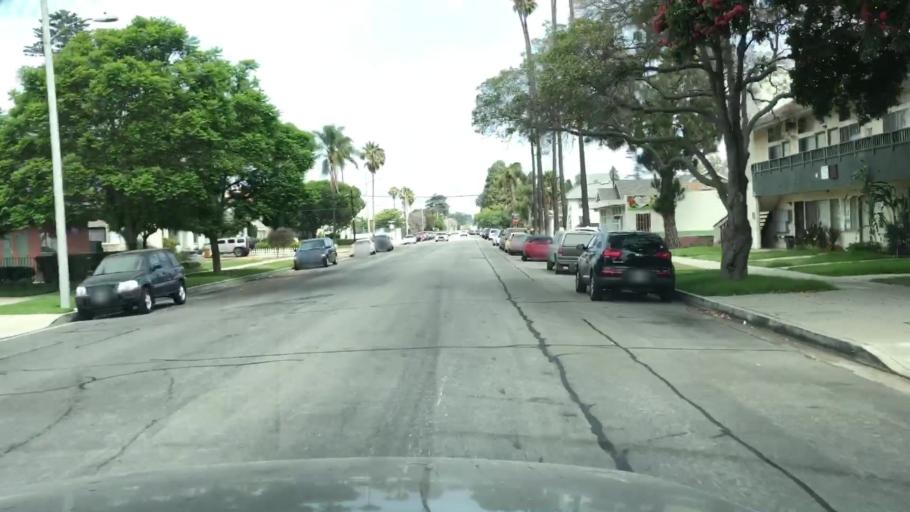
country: US
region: California
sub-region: Ventura County
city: Oxnard
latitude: 34.1981
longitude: -119.1823
